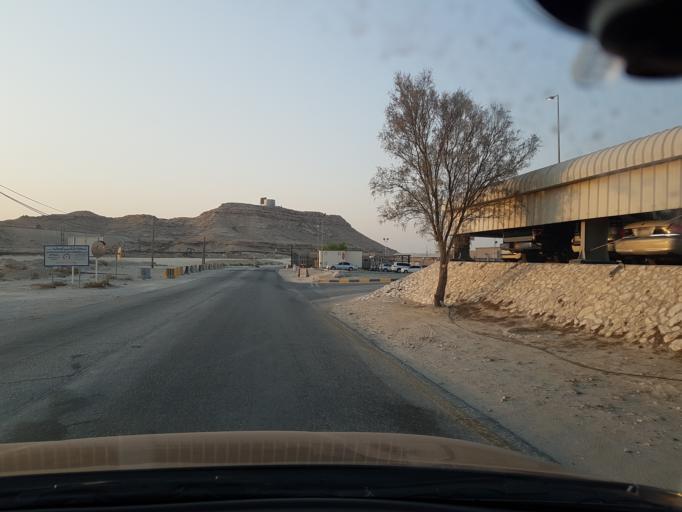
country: BH
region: Central Governorate
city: Dar Kulayb
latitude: 26.0333
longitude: 50.5518
